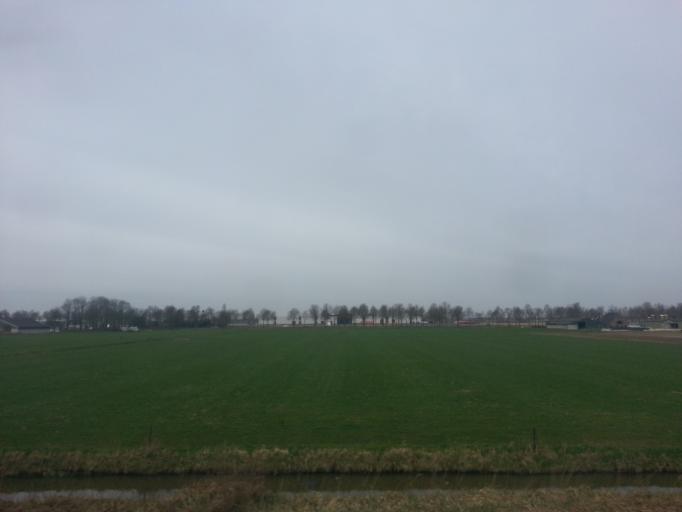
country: NL
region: Gelderland
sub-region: Gemeente Maasdriel
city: Hedel
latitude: 51.7595
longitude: 5.2720
